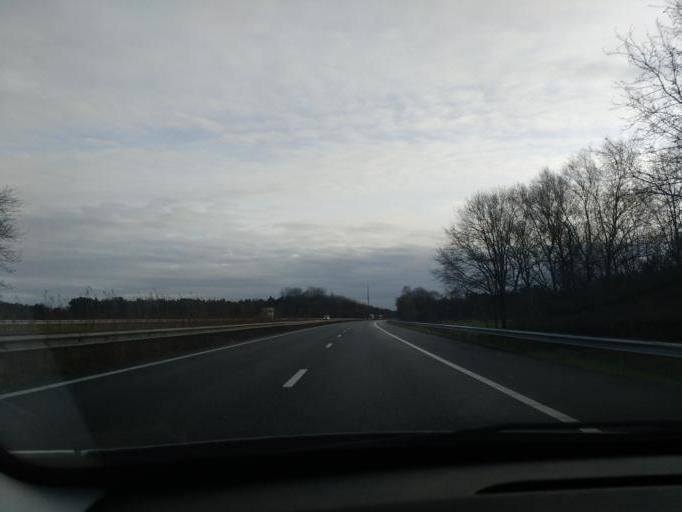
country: NL
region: North Brabant
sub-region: Gemeente Geldrop-Mierlo
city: Mierlo
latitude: 51.4188
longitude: 5.6000
